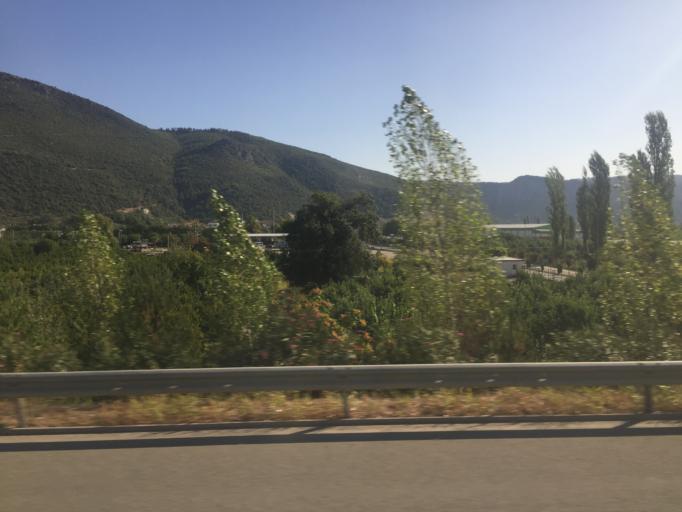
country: TR
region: Bursa
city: Kestel
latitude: 40.2289
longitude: 29.2739
